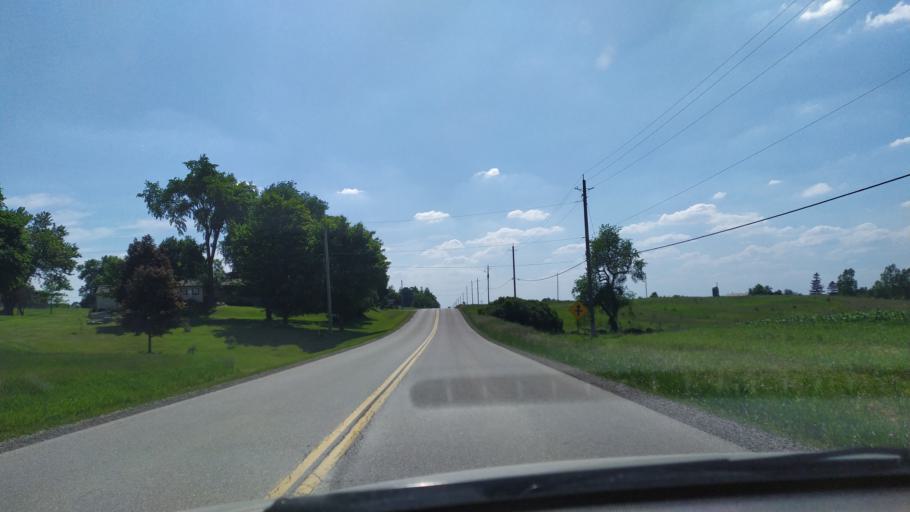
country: CA
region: Ontario
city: Kitchener
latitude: 43.3647
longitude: -80.6019
